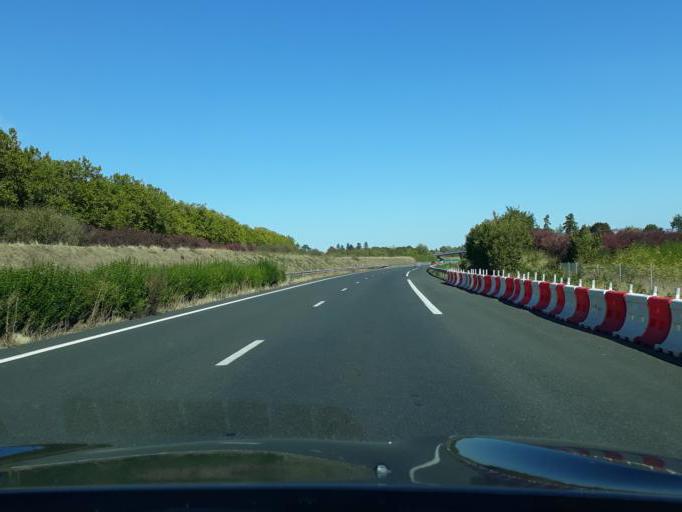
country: FR
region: Centre
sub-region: Departement d'Indre-et-Loire
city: Ballan-Mire
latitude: 47.3305
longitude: 0.6086
